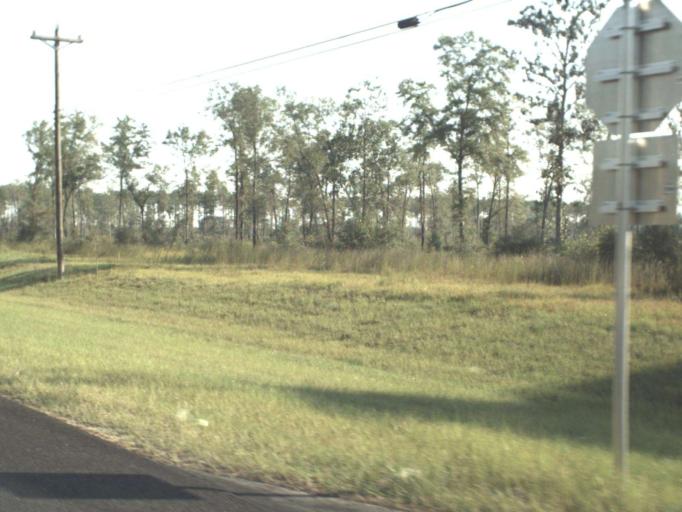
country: US
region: Florida
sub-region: Bay County
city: Laguna Beach
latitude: 30.4807
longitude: -85.8435
